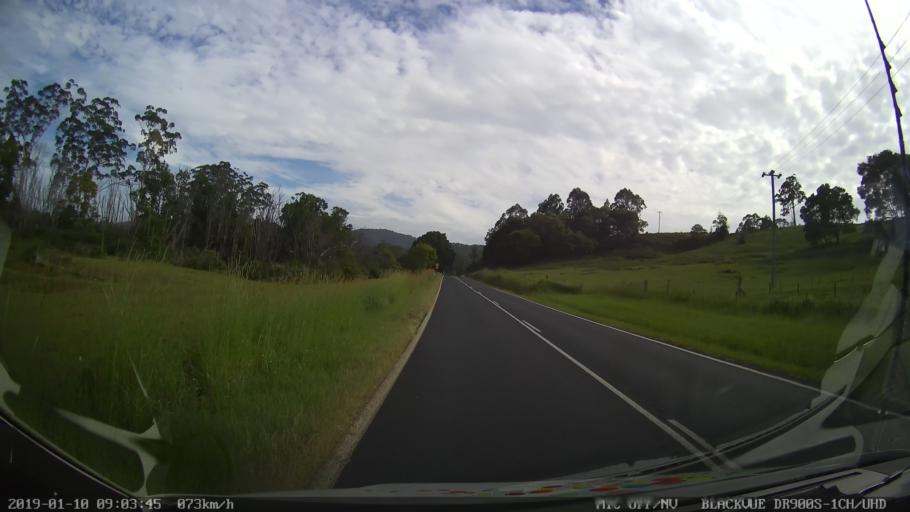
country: AU
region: New South Wales
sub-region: Coffs Harbour
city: Coffs Harbour
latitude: -30.2614
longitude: 153.0495
